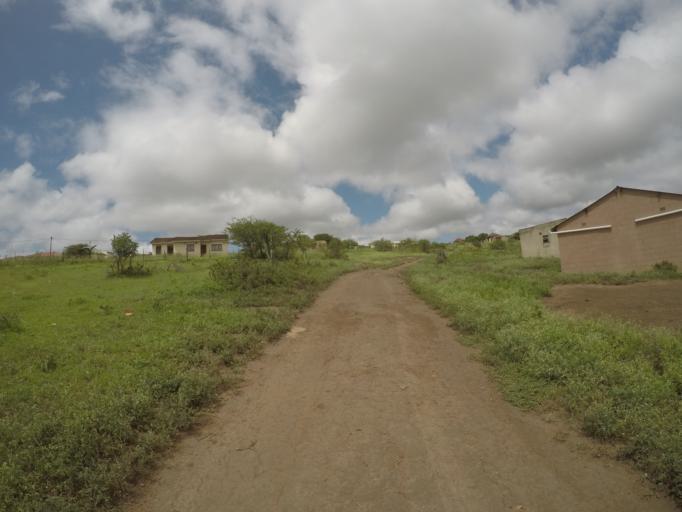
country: ZA
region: KwaZulu-Natal
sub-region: uThungulu District Municipality
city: Empangeni
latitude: -28.5742
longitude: 31.8419
